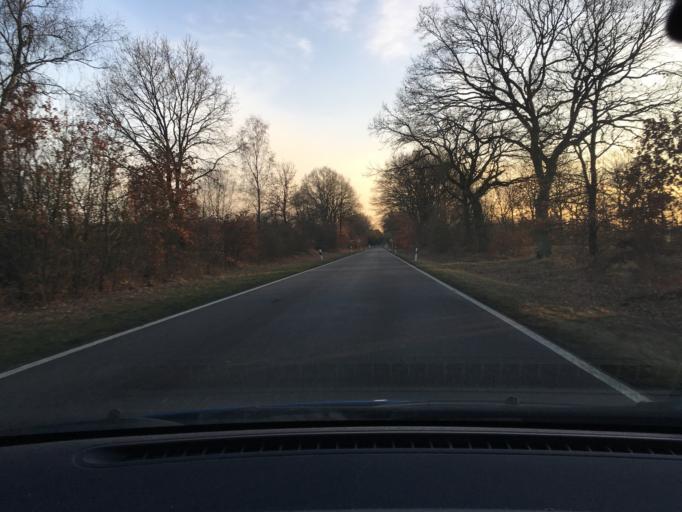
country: DE
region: Schleswig-Holstein
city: Langenlehsten
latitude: 53.5074
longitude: 10.7426
